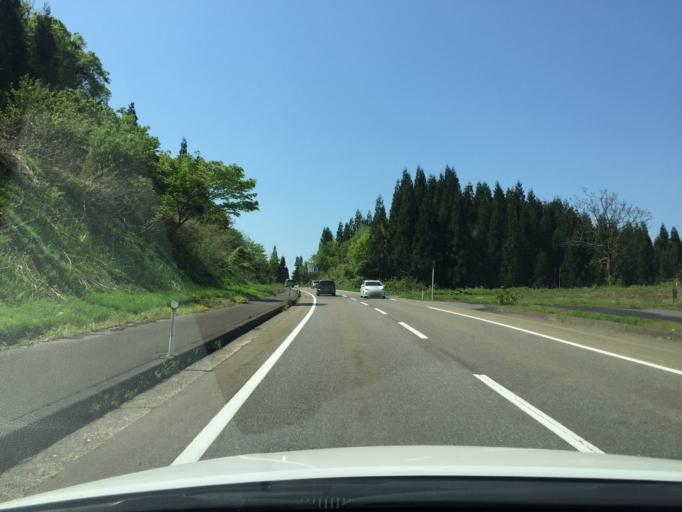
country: JP
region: Niigata
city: Kamo
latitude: 37.5944
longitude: 139.0933
